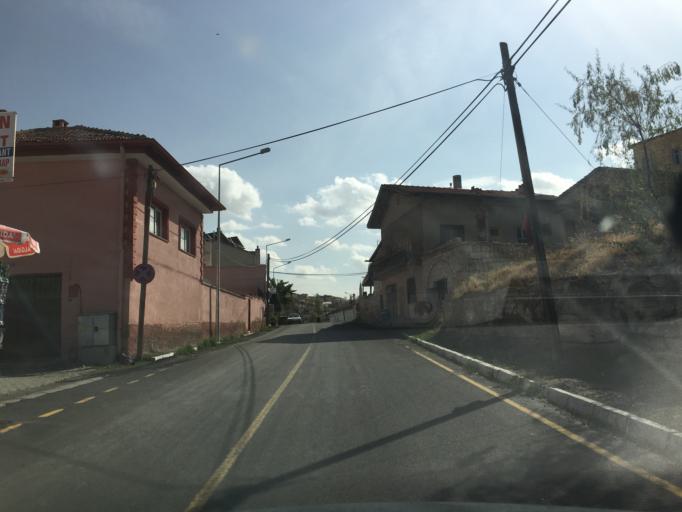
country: TR
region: Nevsehir
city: Goereme
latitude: 38.6702
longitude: 34.8407
